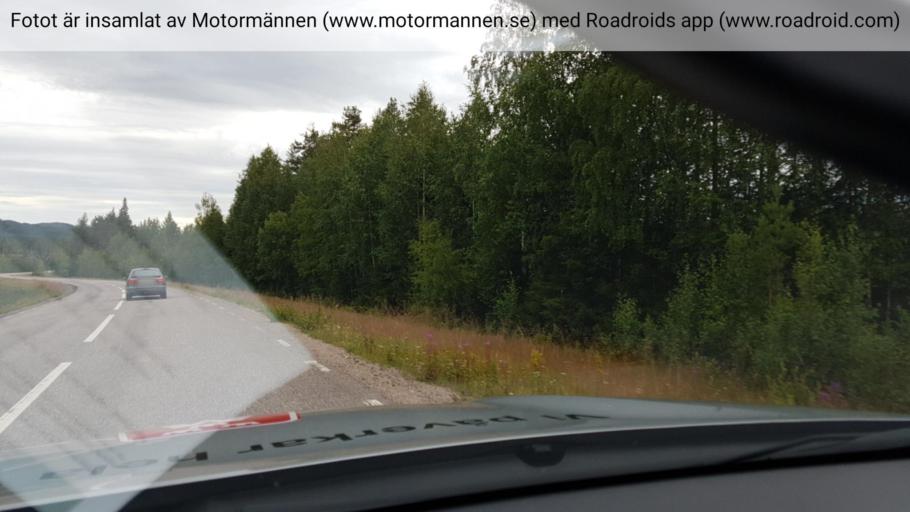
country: SE
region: Norrbotten
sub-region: Overkalix Kommun
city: OEverkalix
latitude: 66.6212
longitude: 22.7675
